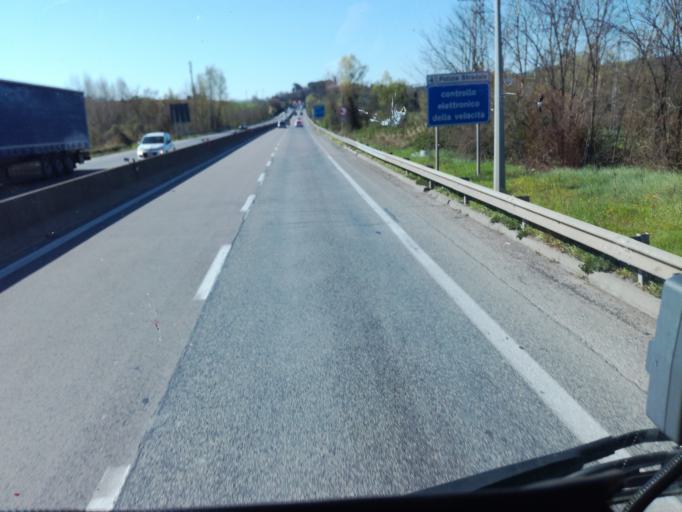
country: IT
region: Umbria
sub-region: Provincia di Perugia
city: Via Lippia
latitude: 43.0969
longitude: 12.4758
